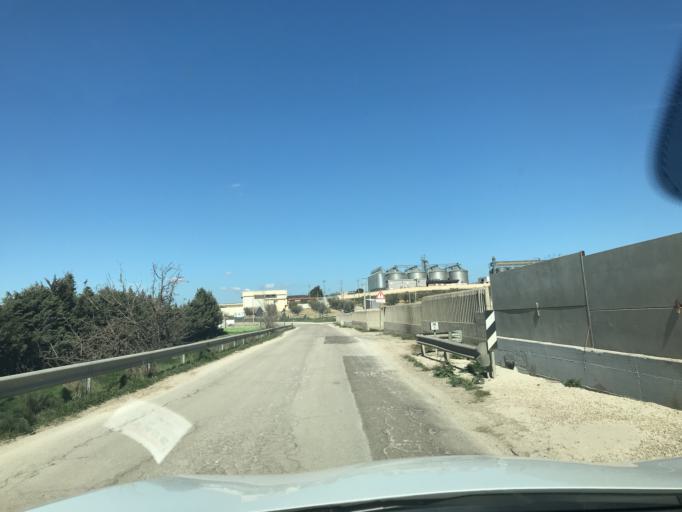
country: IT
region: Apulia
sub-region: Provincia di Bari
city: Gravina in Puglia
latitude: 40.8387
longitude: 16.4273
